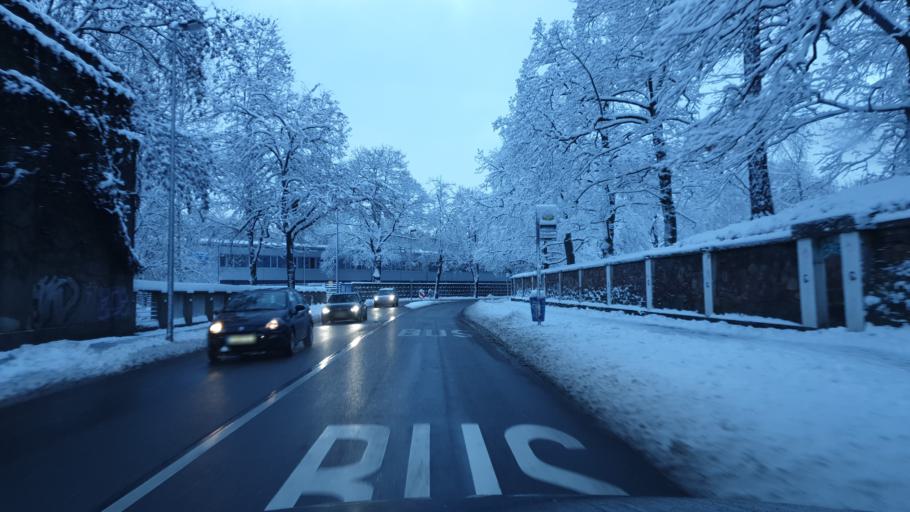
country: DE
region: Saxony
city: Chemnitz
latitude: 50.8495
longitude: 12.9212
